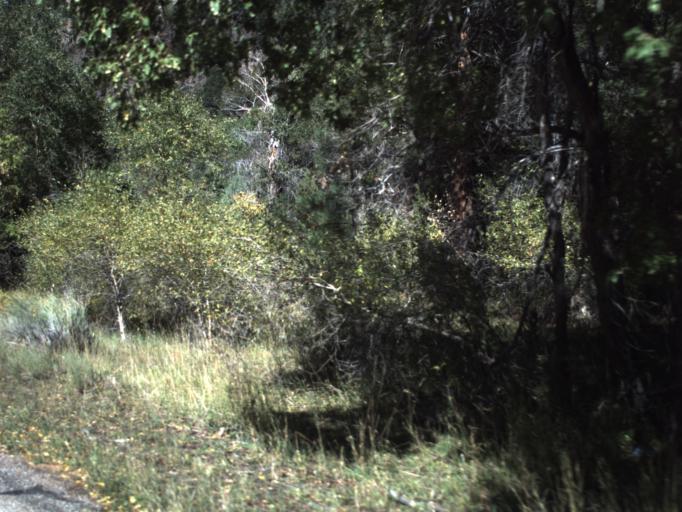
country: US
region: Utah
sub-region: Beaver County
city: Beaver
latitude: 38.2640
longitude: -112.5476
